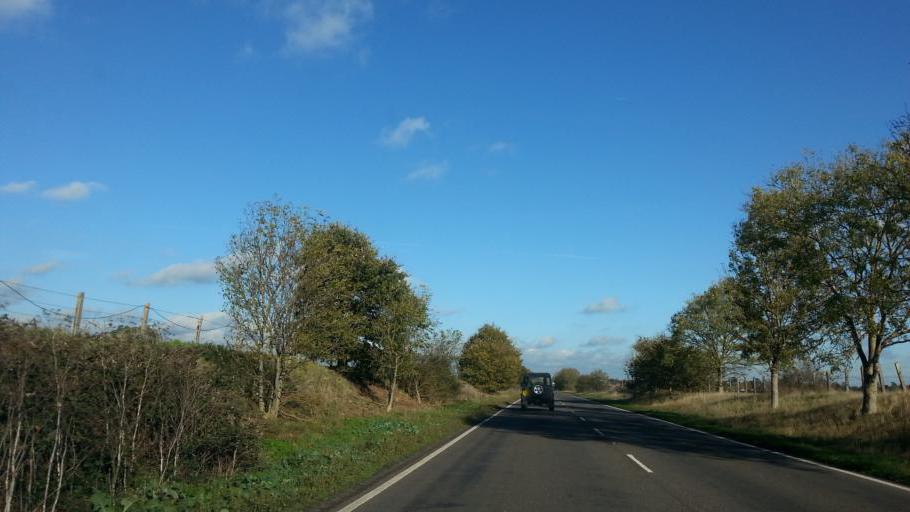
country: GB
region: England
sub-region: Suffolk
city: Bungay
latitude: 52.4451
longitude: 1.4032
